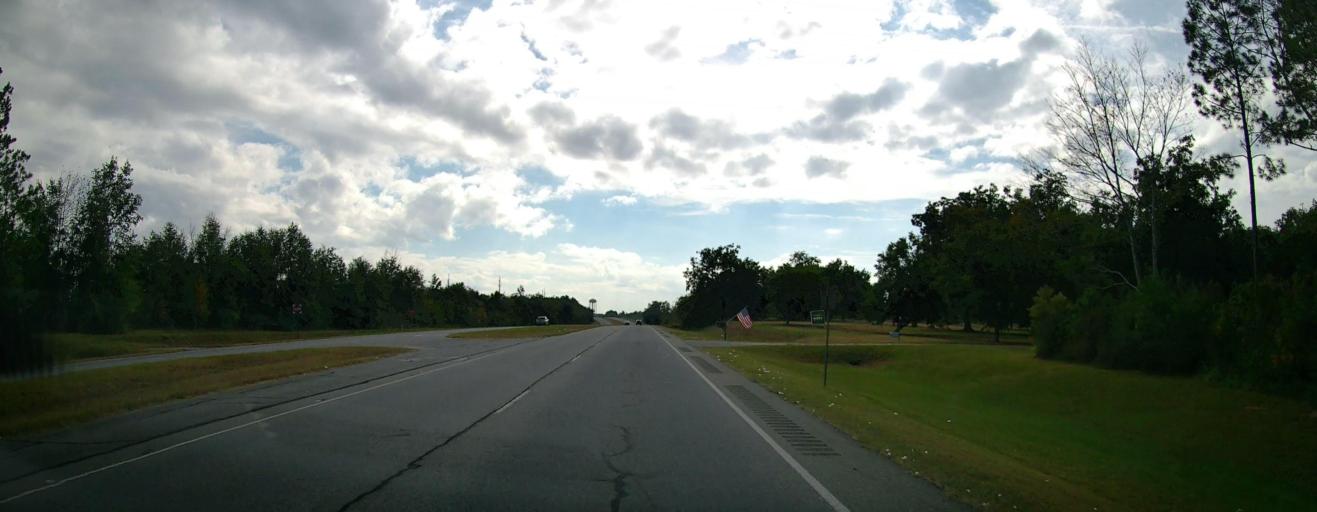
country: US
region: Georgia
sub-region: Mitchell County
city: Camilla
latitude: 31.2958
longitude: -84.1832
